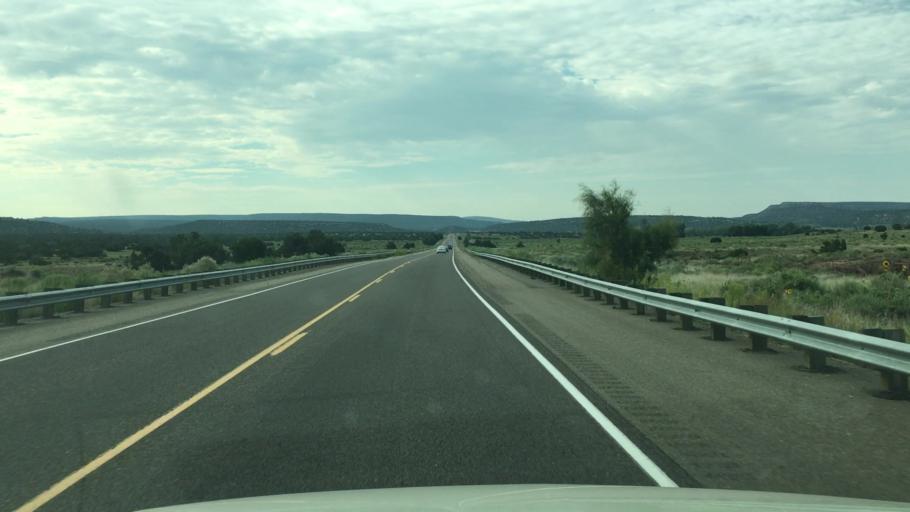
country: US
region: New Mexico
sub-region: Santa Fe County
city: Eldorado at Santa Fe
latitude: 35.4121
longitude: -105.8672
